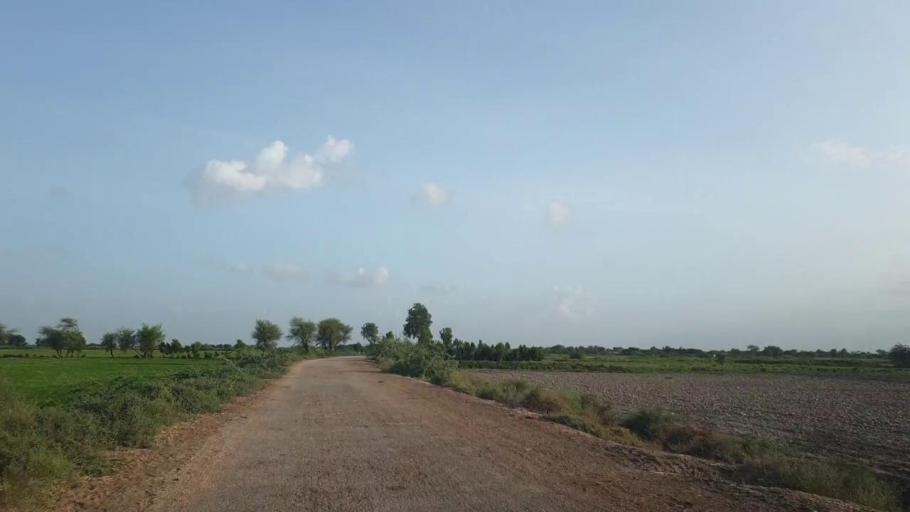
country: PK
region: Sindh
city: Kadhan
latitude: 24.6348
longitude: 69.1227
